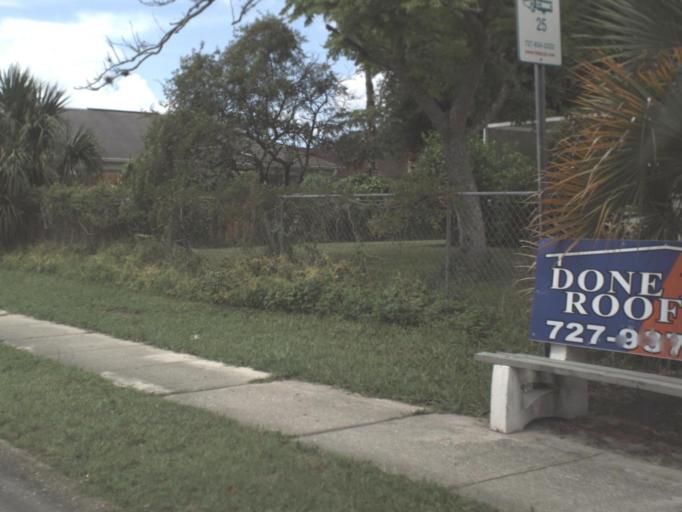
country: US
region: Florida
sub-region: Pasco County
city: Elfers
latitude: 28.2143
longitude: -82.6928
